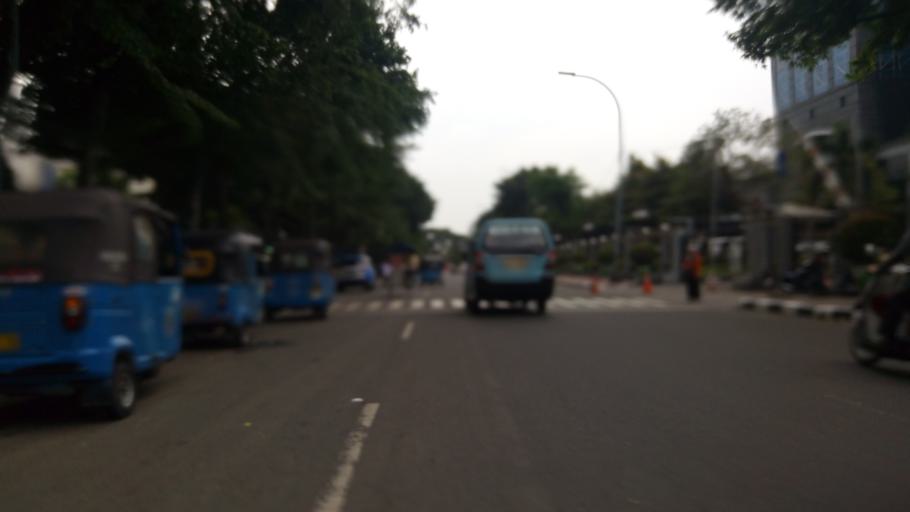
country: ID
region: Jakarta Raya
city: Jakarta
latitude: -6.1729
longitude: 106.8377
